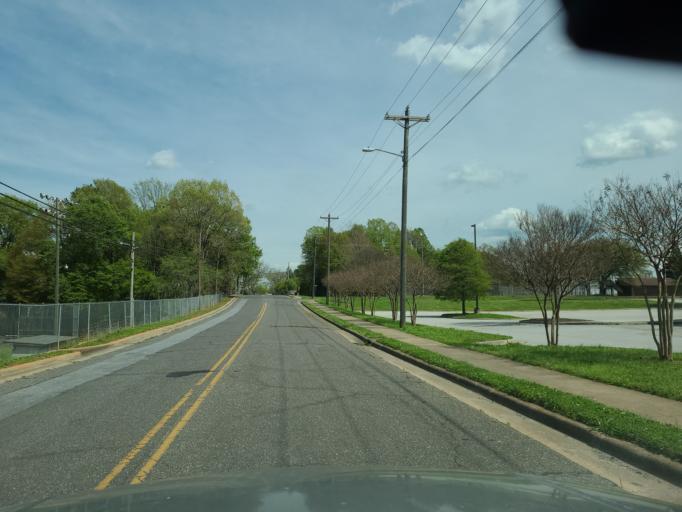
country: US
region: North Carolina
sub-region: Cleveland County
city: Shelby
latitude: 35.2935
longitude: -81.5445
